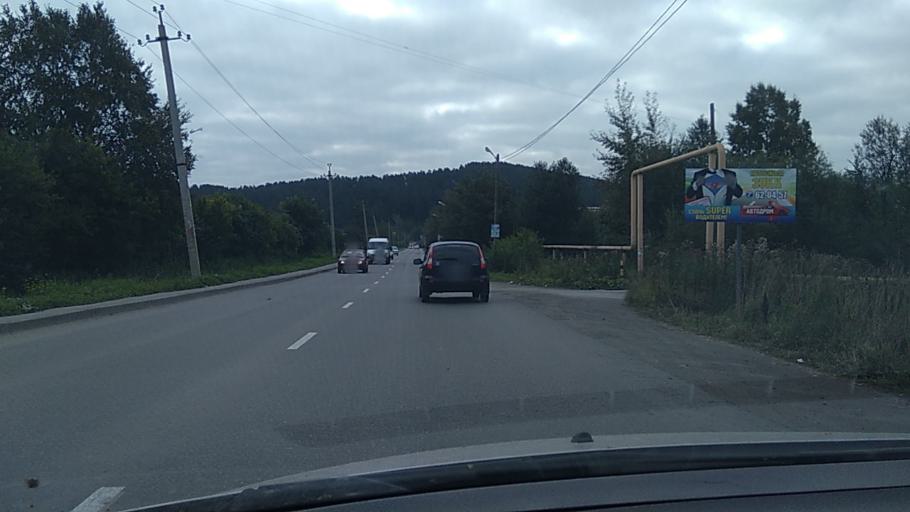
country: RU
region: Chelyabinsk
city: Zlatoust
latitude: 55.1767
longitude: 59.7041
